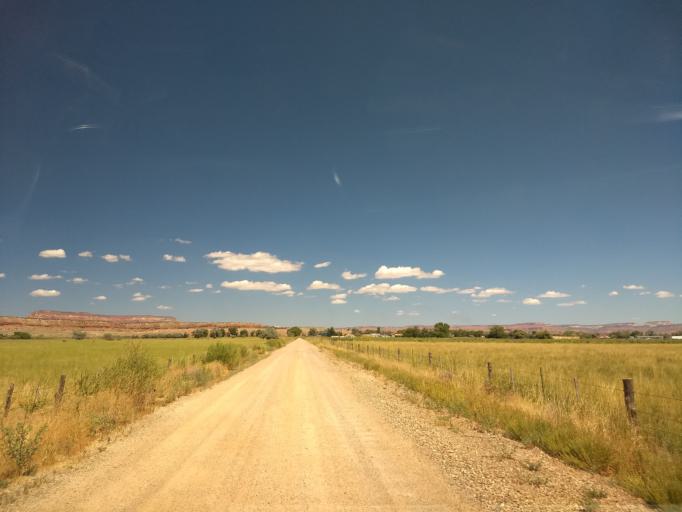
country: US
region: Arizona
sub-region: Coconino County
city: Fredonia
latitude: 36.9275
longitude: -112.5399
